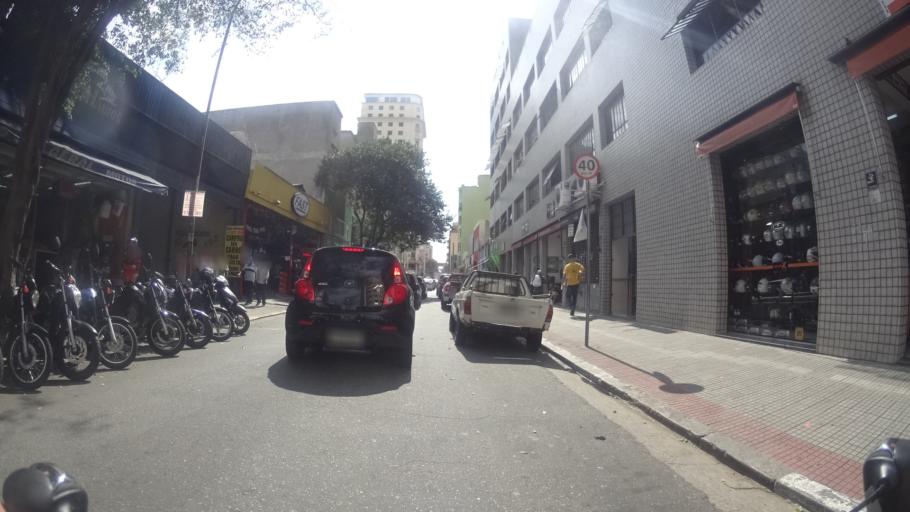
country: BR
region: Sao Paulo
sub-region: Sao Paulo
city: Sao Paulo
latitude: -23.5387
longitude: -46.6431
